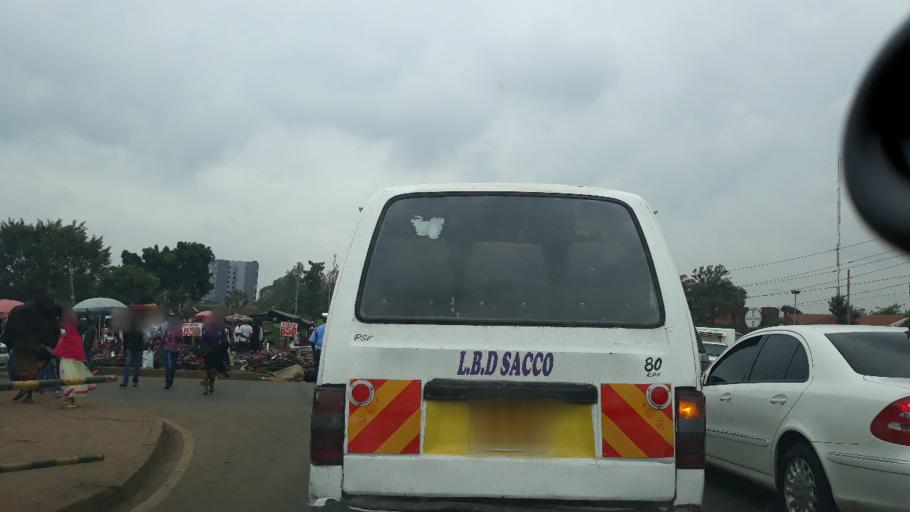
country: KE
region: Nairobi Area
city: Pumwani
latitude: -1.2449
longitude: 36.8671
